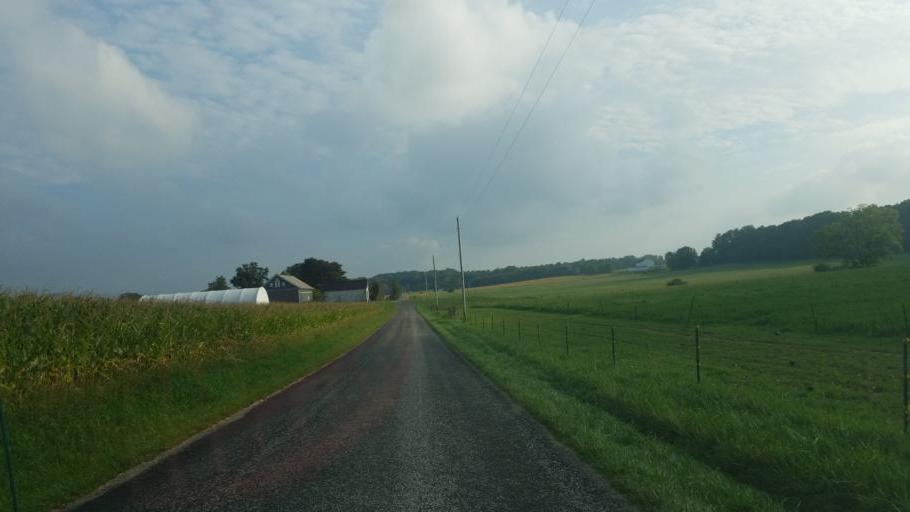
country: US
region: Ohio
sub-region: Wayne County
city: Wooster
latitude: 40.8646
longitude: -82.0295
